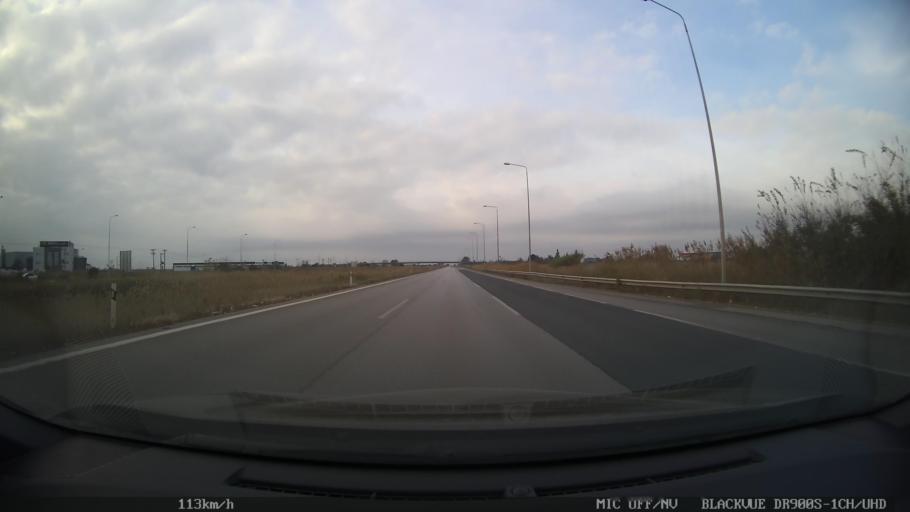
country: GR
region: Central Macedonia
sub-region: Nomos Thessalonikis
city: Sindos
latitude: 40.6481
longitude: 22.8067
